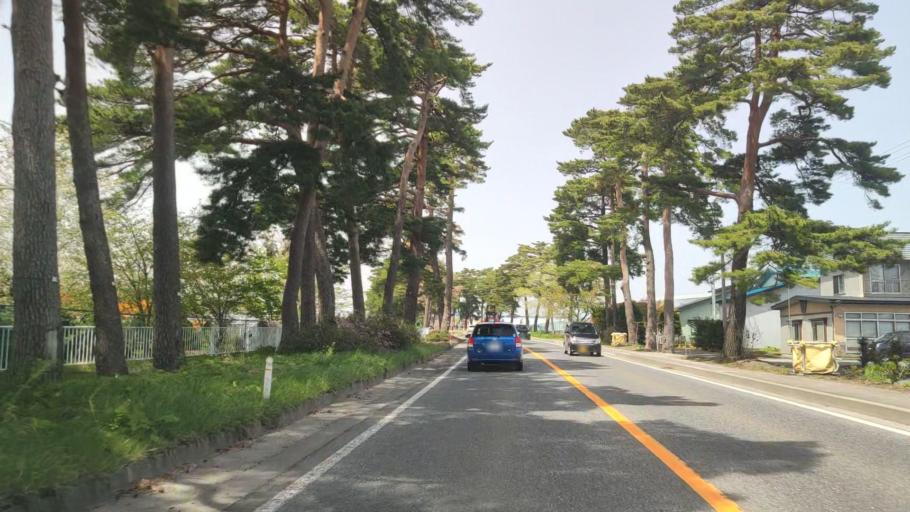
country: JP
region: Aomori
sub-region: Misawa Shi
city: Inuotose
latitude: 40.6708
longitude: 141.1835
